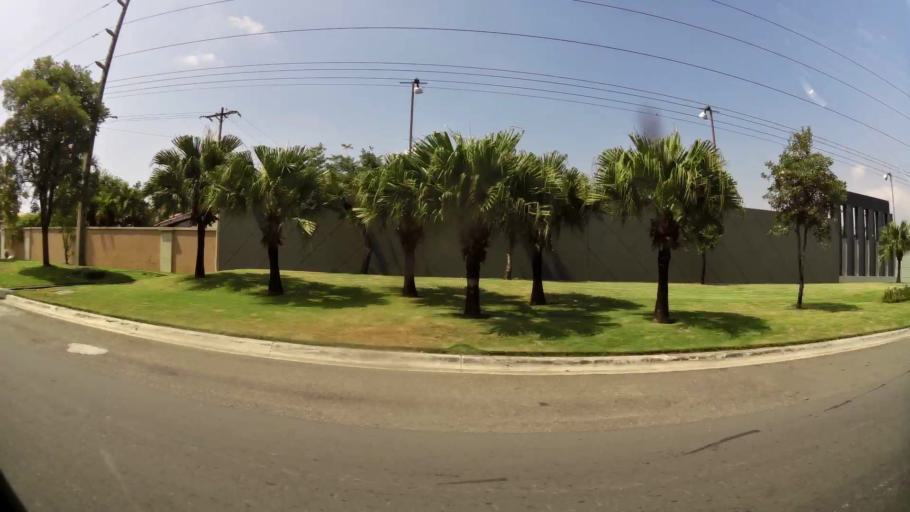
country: EC
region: Guayas
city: Eloy Alfaro
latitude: -2.0896
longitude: -79.8735
